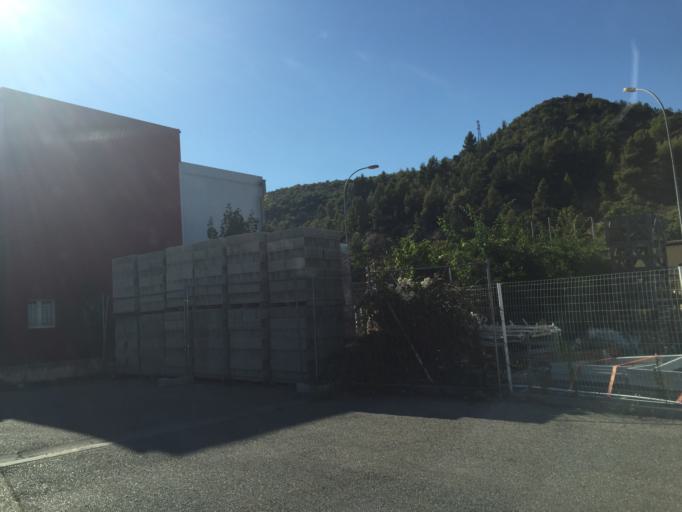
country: FR
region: Provence-Alpes-Cote d'Azur
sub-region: Departement des Alpes-de-Haute-Provence
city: Digne-les-Bains
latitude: 44.0782
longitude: 6.1917
